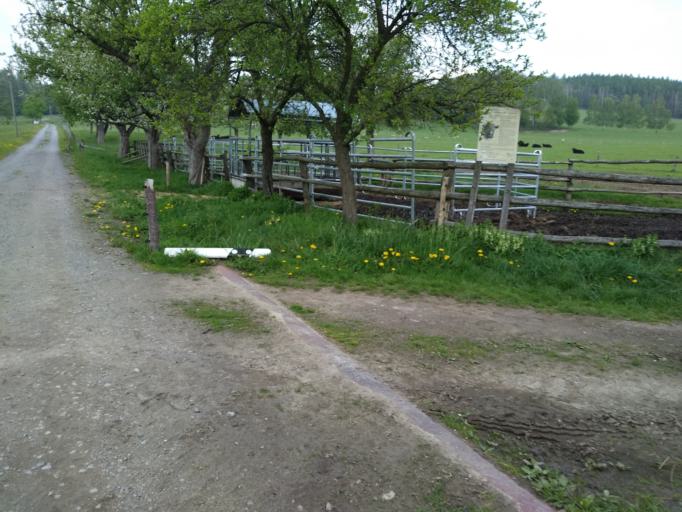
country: DE
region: Saxony
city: Porschdorf
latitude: 50.9562
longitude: 14.1390
